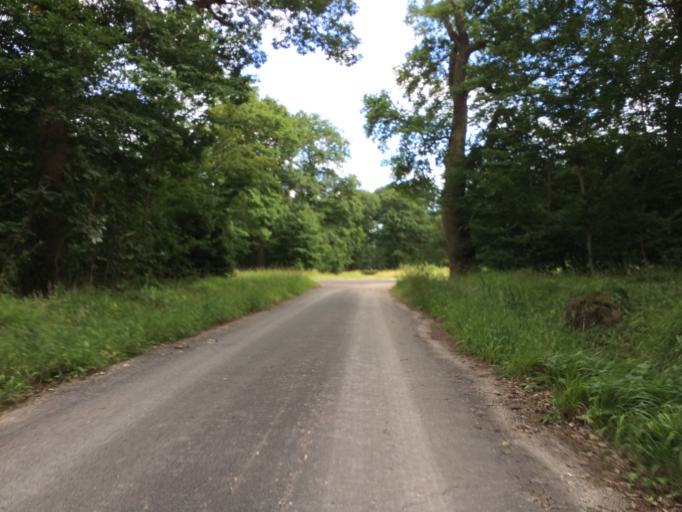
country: FR
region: Ile-de-France
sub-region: Departement de l'Essonne
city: Etiolles
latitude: 48.6582
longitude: 2.4868
